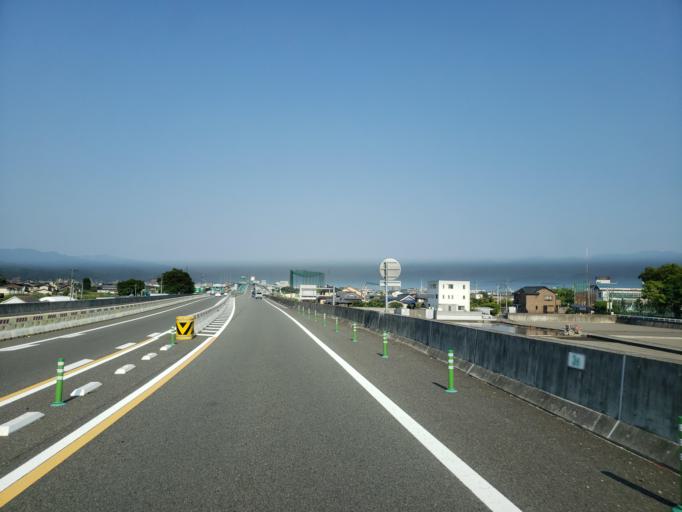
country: JP
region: Ehime
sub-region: Shikoku-chuo Shi
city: Matsuyama
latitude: 33.8023
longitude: 132.7658
